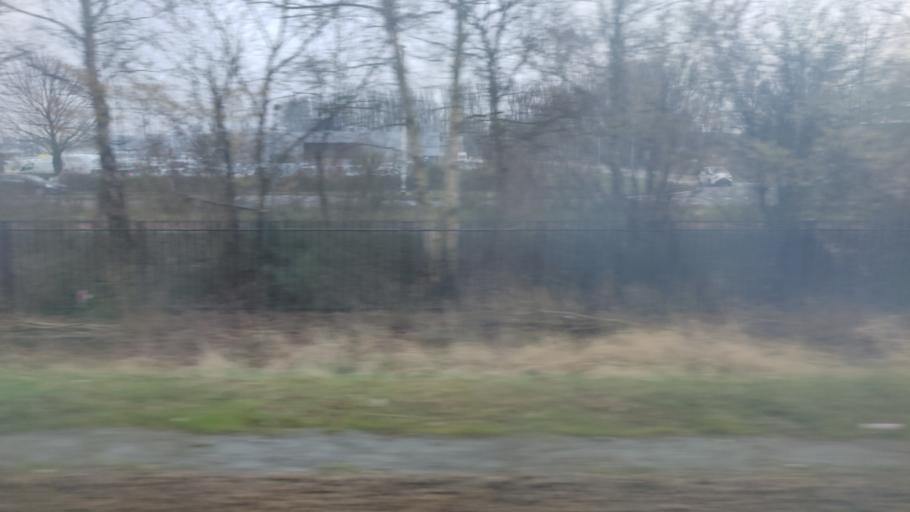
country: NL
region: North Holland
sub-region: Gemeente Alkmaar
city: Alkmaar
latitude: 52.6454
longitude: 4.7677
